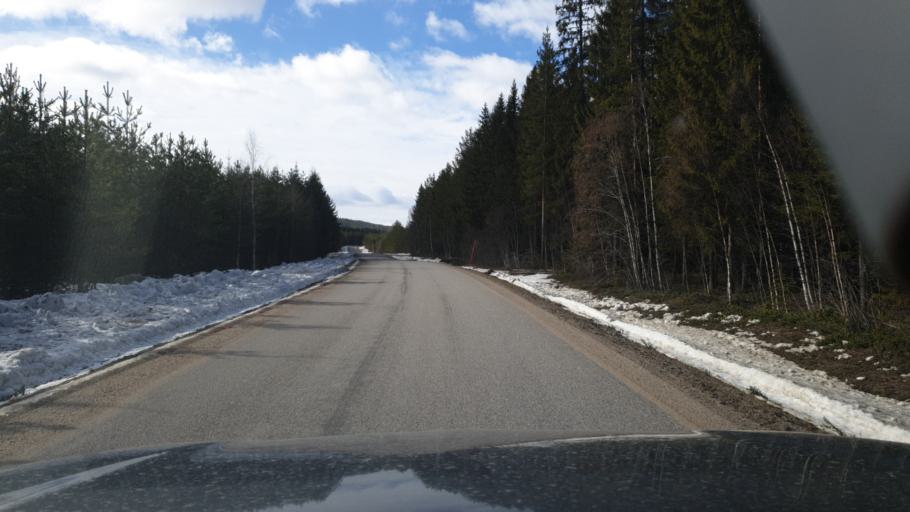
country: SE
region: Gaevleborg
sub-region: Ljusdals Kommun
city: Farila
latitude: 61.8466
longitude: 15.9615
